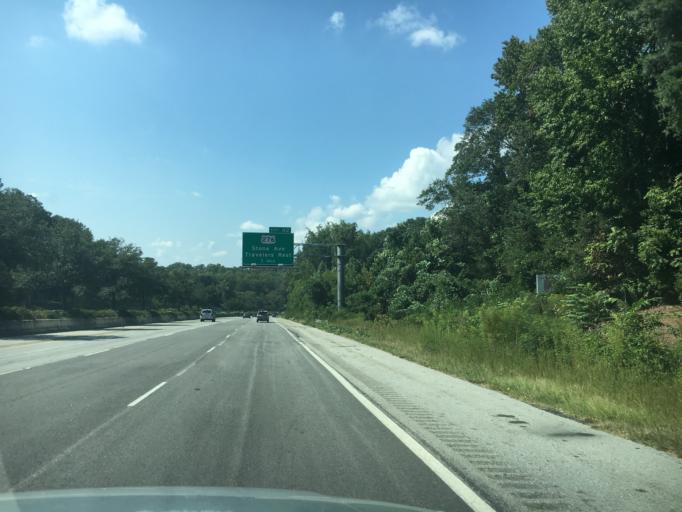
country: US
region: South Carolina
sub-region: Greenville County
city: Greenville
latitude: 34.8535
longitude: -82.3642
